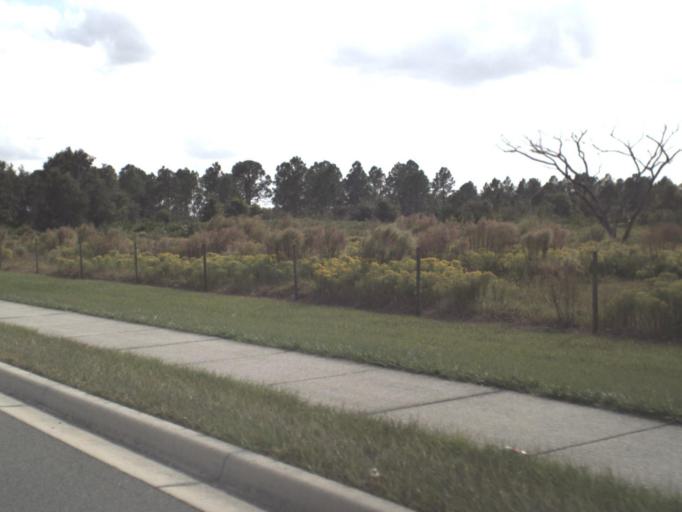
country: US
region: Florida
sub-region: Osceola County
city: Buenaventura Lakes
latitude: 28.3585
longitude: -81.2424
